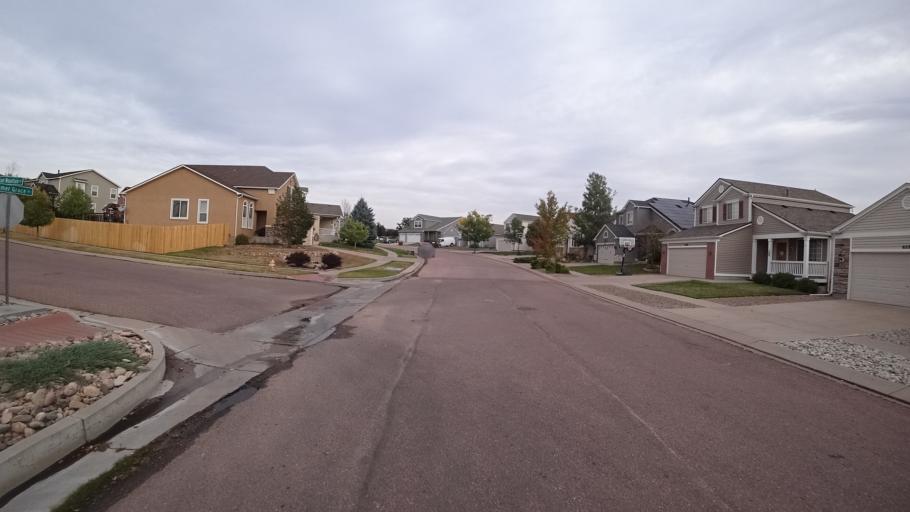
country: US
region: Colorado
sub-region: El Paso County
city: Cimarron Hills
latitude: 38.9176
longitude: -104.7007
